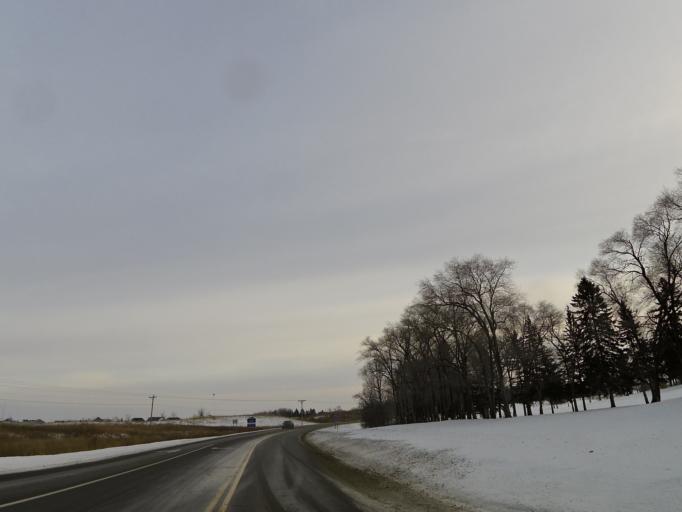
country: US
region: Minnesota
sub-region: Carver County
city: Victoria
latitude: 44.8488
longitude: -93.6566
